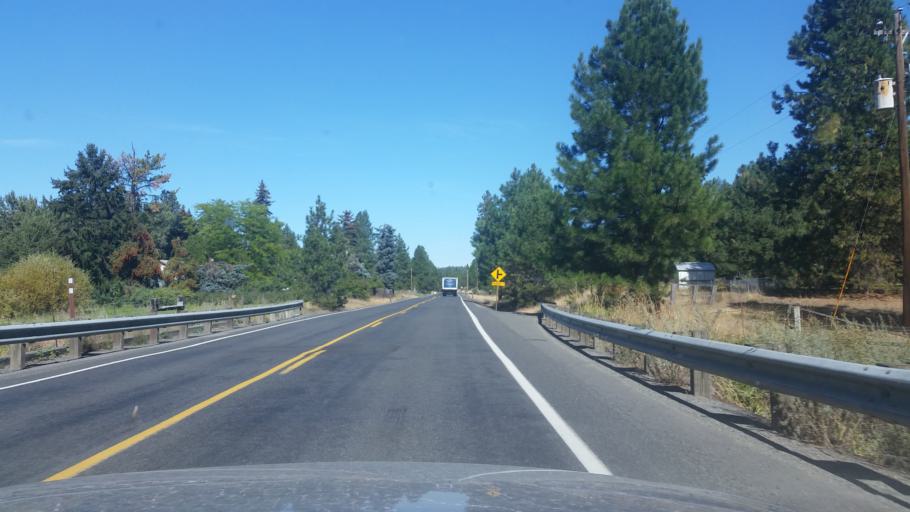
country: US
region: Washington
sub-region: Spokane County
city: Spokane
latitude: 47.5782
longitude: -117.4628
